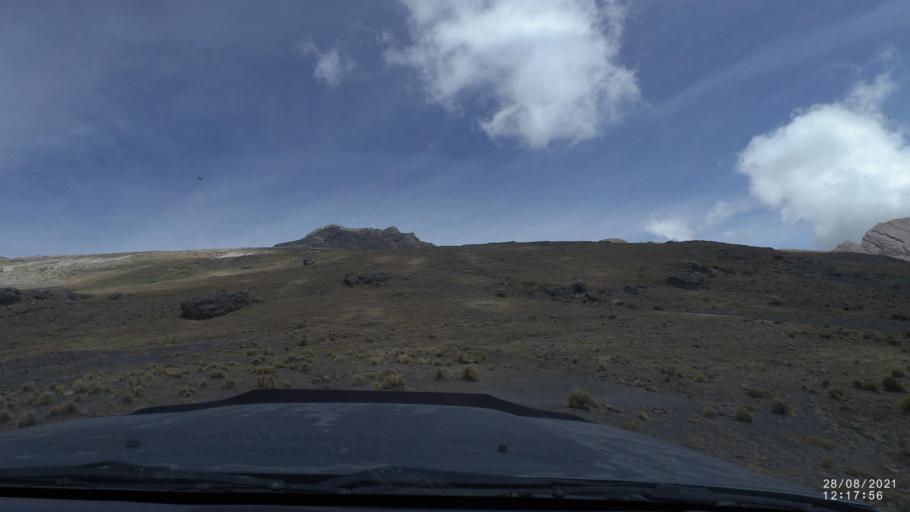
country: BO
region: Cochabamba
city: Sipe Sipe
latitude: -17.2785
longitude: -66.3813
